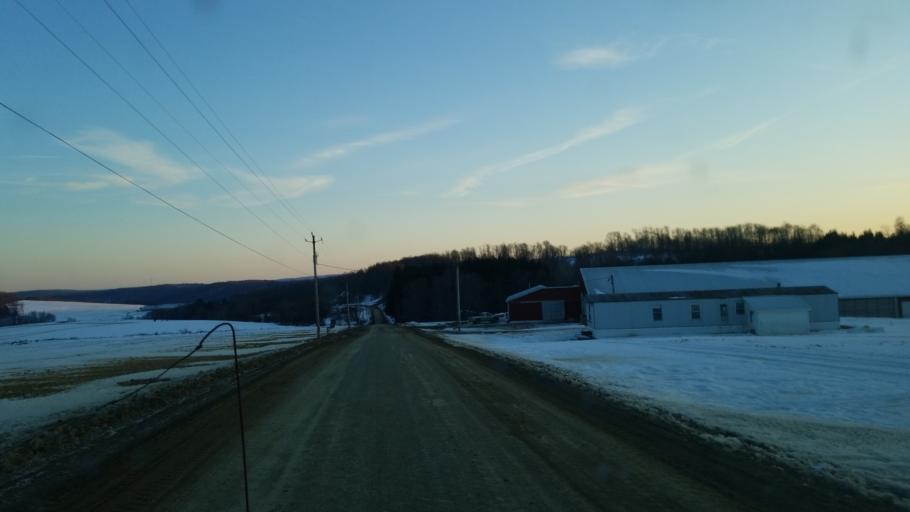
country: US
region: Pennsylvania
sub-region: Tioga County
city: Westfield
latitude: 42.0200
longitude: -77.6567
